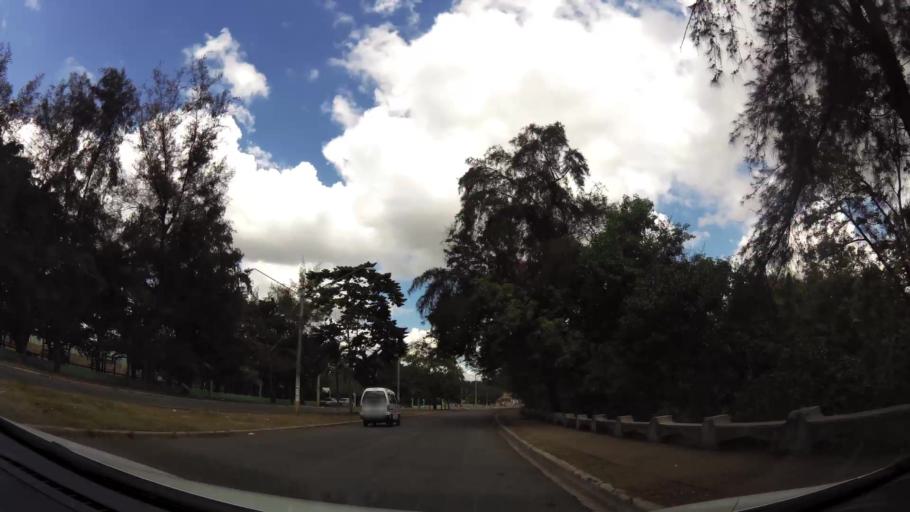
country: DO
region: Santo Domingo
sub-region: Santo Domingo
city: Santo Domingo Este
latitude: 18.4794
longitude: -69.8444
